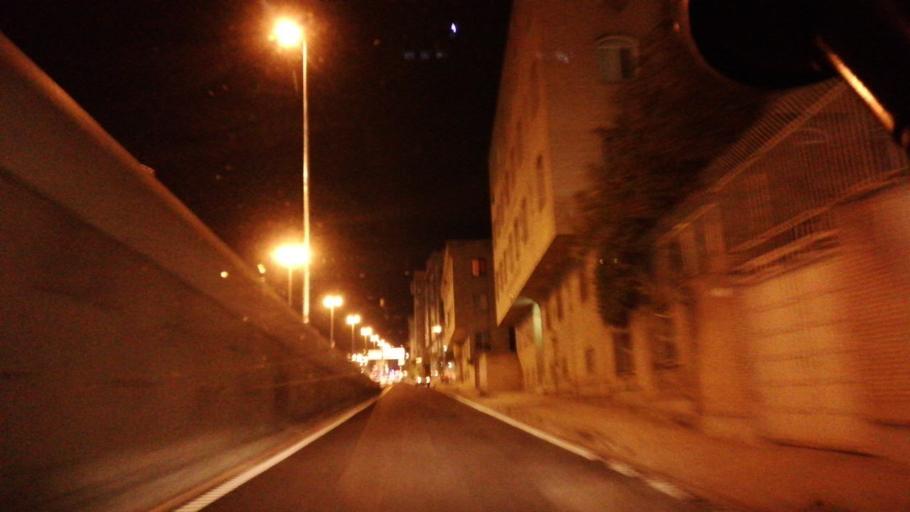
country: IR
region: Tehran
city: Tajrish
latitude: 35.7922
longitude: 51.4879
